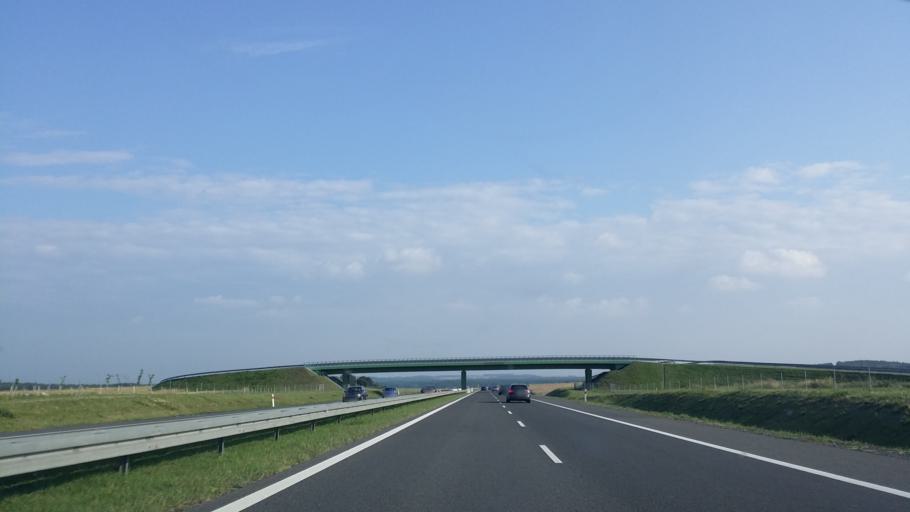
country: PL
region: Lubusz
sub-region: Powiat miedzyrzecki
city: Miedzyrzecz
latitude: 52.3608
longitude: 15.5510
